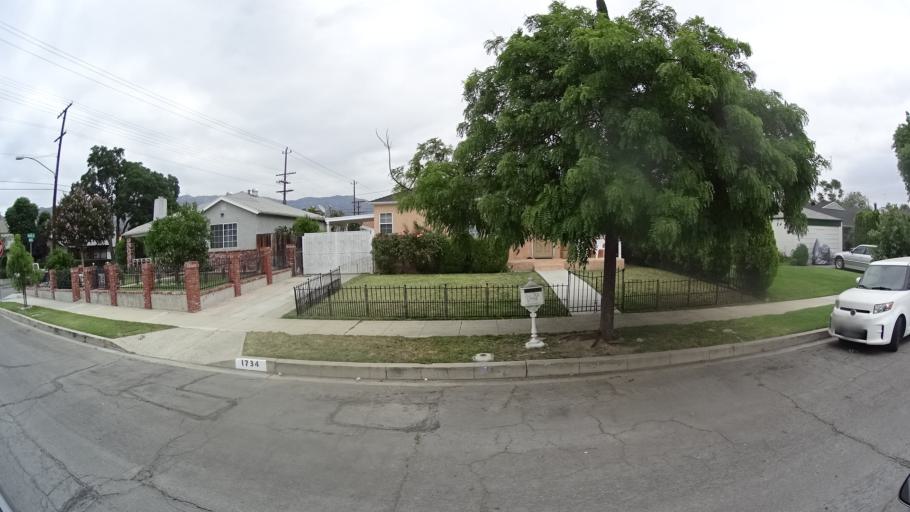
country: US
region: California
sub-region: Los Angeles County
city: Burbank
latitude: 34.1880
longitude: -118.3371
